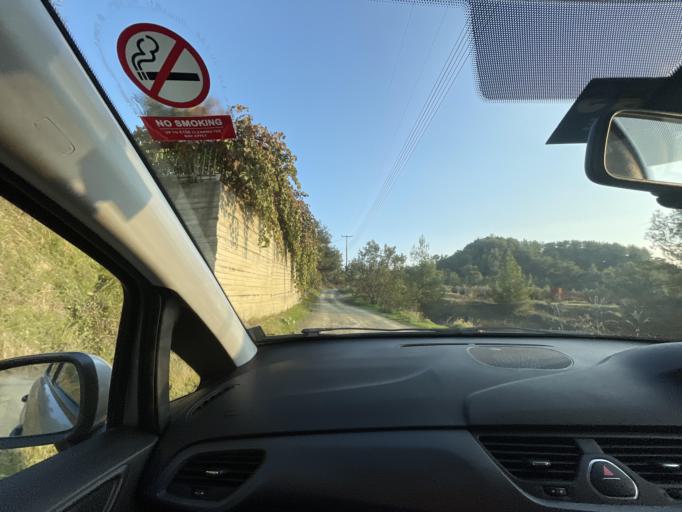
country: CY
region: Limassol
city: Pelendri
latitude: 34.8873
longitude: 32.9730
